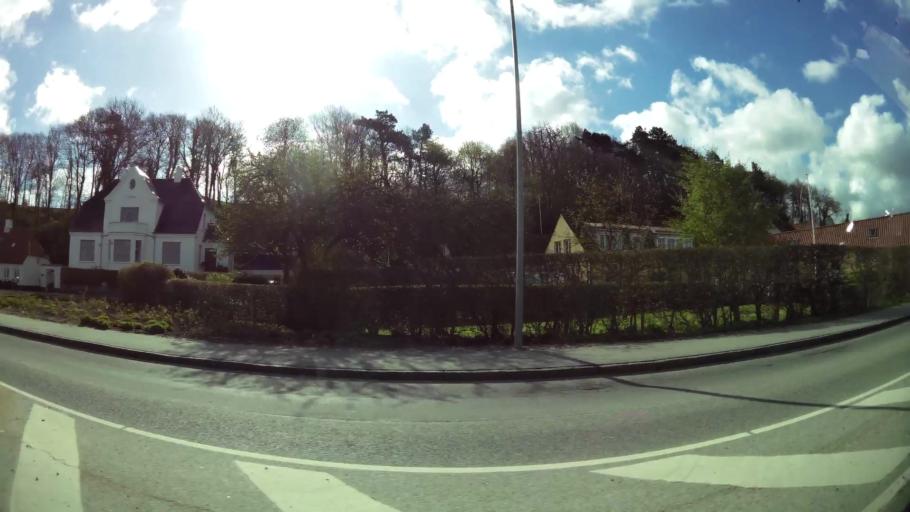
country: DK
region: North Denmark
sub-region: Mariagerfjord Kommune
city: Mariager
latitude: 56.6538
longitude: 9.9848
